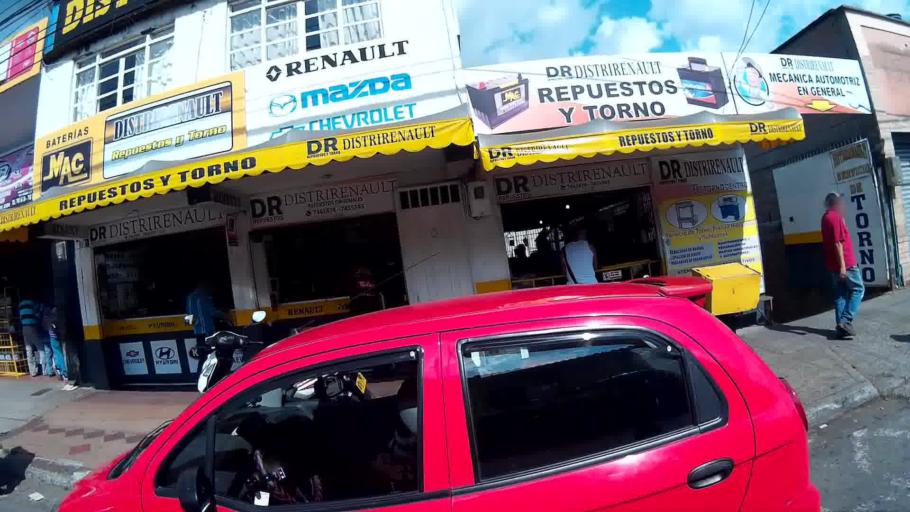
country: CO
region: Quindio
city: Armenia
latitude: 4.5393
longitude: -75.6722
